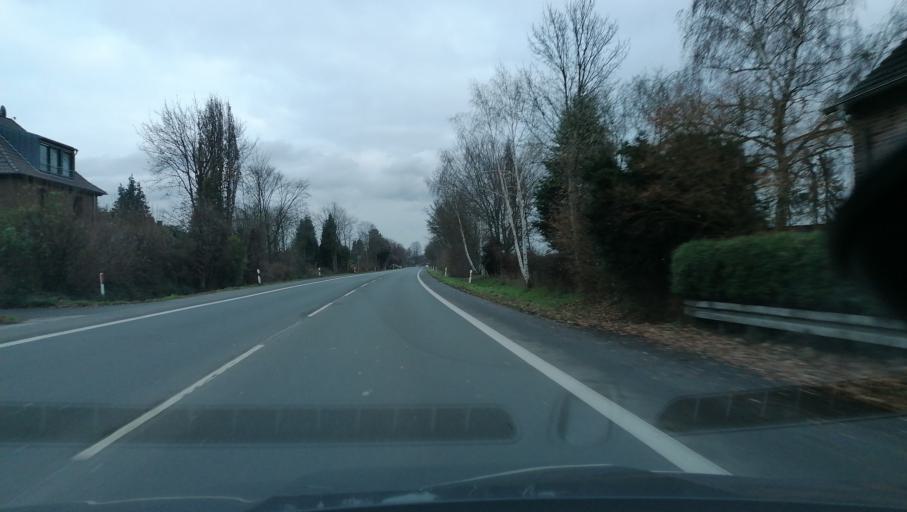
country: DE
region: North Rhine-Westphalia
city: Marl
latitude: 51.6518
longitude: 7.0633
